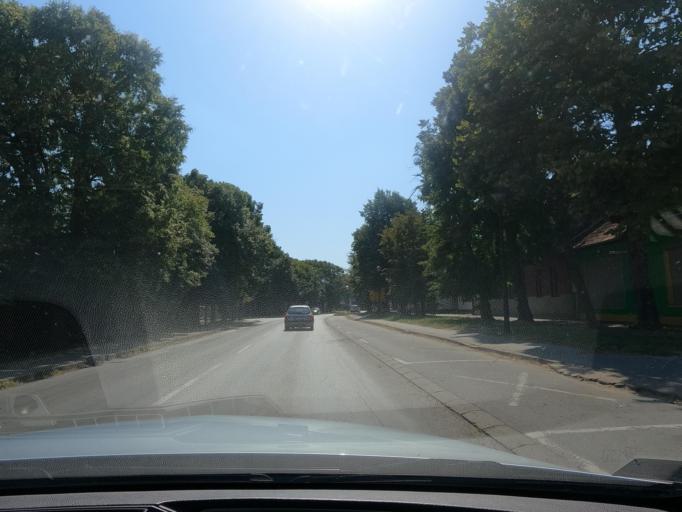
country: RS
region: Autonomna Pokrajina Vojvodina
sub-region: Severnobacki Okrug
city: Backa Topola
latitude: 45.8160
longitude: 19.6446
